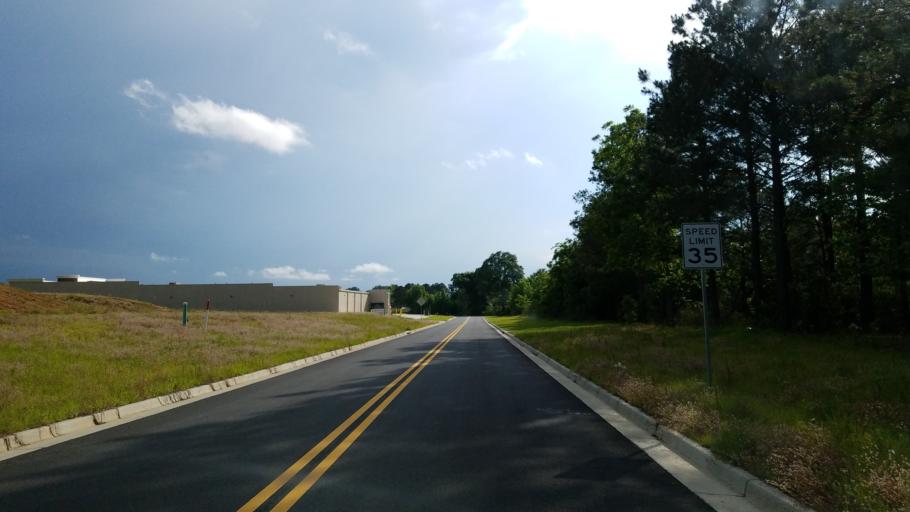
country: US
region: Georgia
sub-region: Tift County
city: Tifton
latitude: 31.4486
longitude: -83.5423
